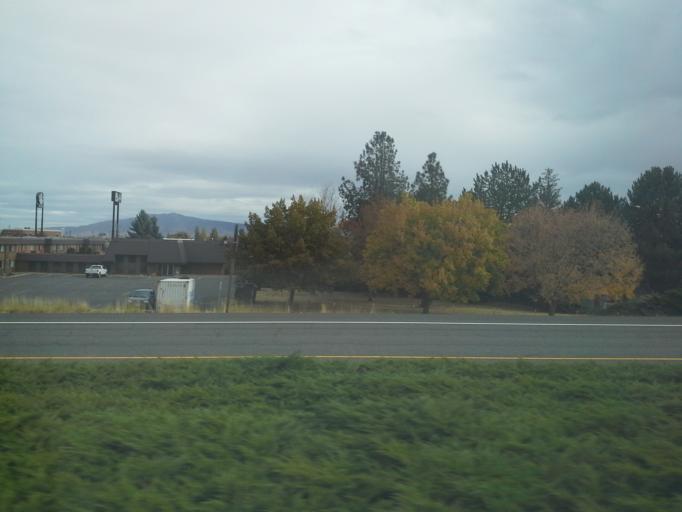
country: US
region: Oregon
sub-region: Union County
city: La Grande
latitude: 45.3312
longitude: -118.0700
